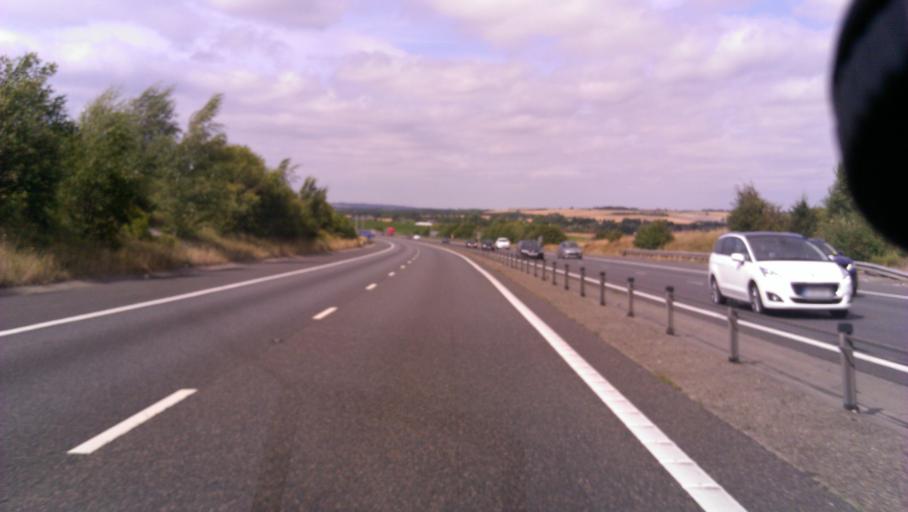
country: GB
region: England
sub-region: Essex
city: Saffron Walden
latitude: 52.0482
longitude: 0.1923
